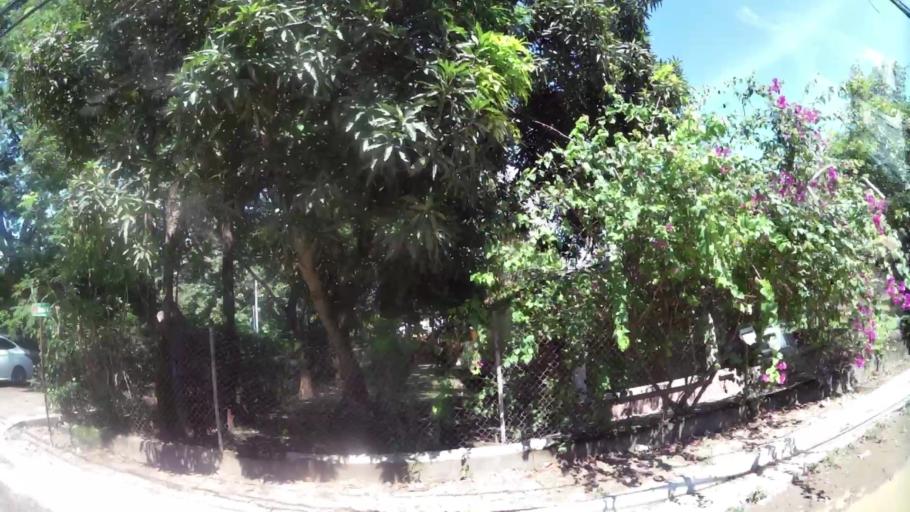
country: PA
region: Panama
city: Nueva Gorgona
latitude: 8.5556
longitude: -79.8620
